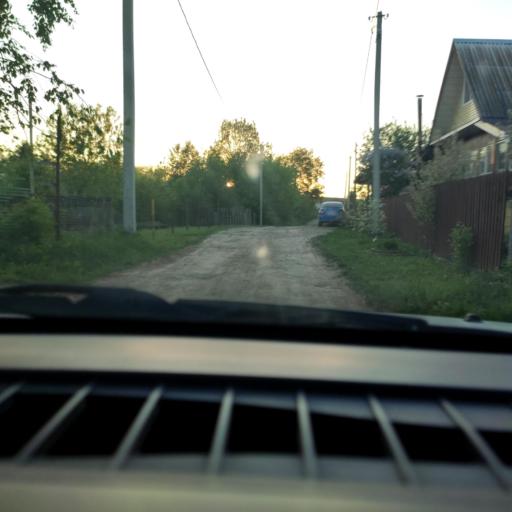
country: RU
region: Perm
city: Froly
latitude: 57.9293
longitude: 56.2857
